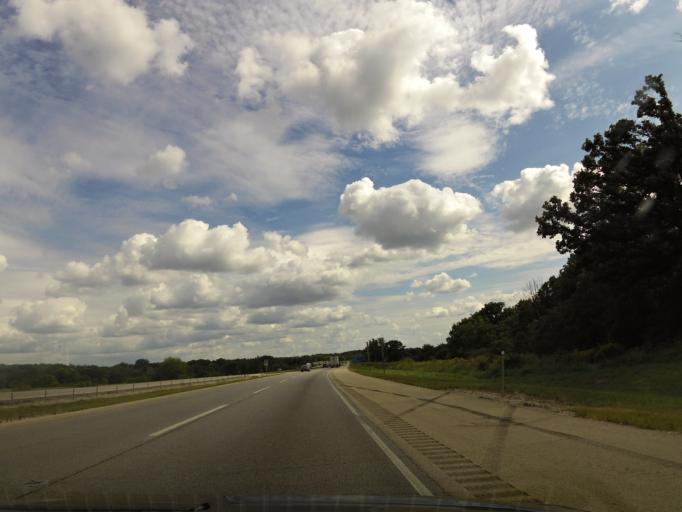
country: US
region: Illinois
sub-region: Kane County
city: Elburn
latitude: 41.8284
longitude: -88.4799
